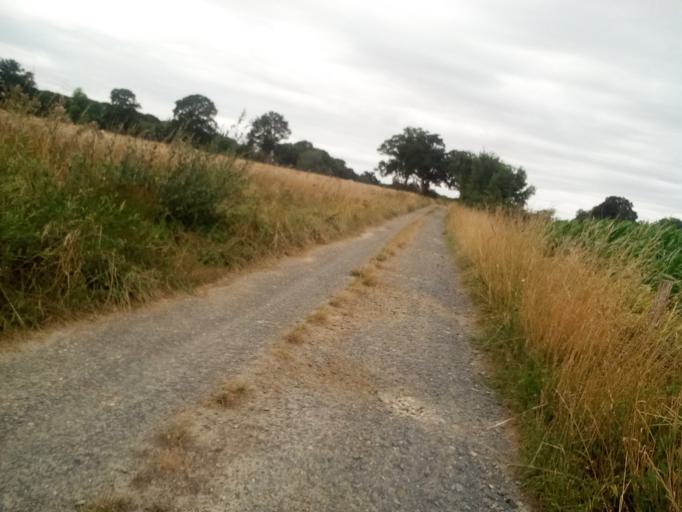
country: FR
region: Lower Normandy
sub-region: Departement du Calvados
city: Clinchamps-sur-Orne
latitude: 49.0412
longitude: -0.3959
